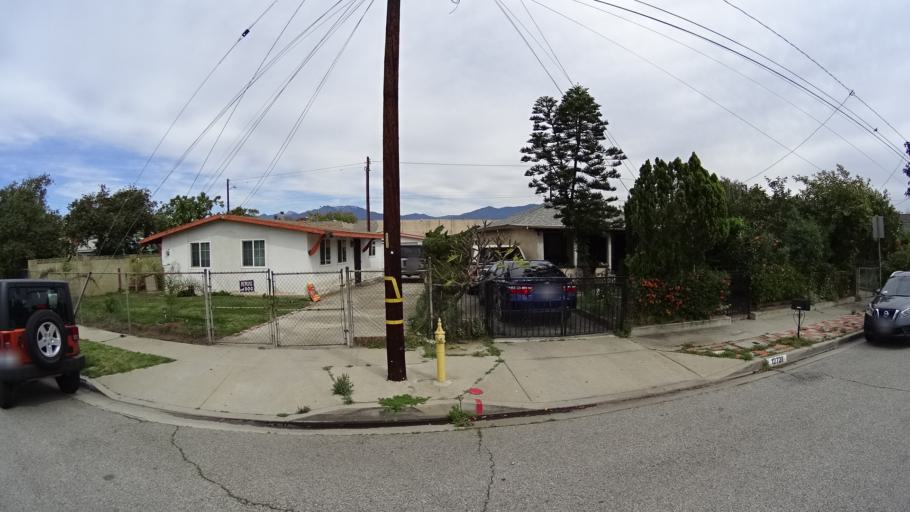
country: US
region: California
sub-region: Los Angeles County
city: El Monte
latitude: 34.0774
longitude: -117.9951
